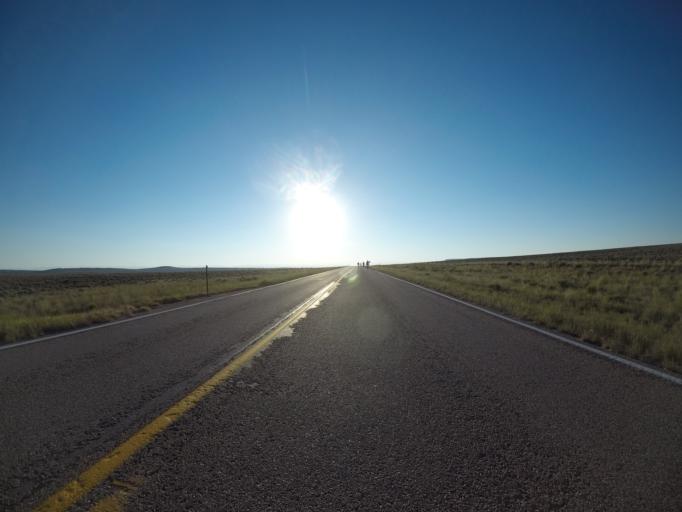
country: US
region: Wyoming
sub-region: Sublette County
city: Marbleton
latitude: 42.5790
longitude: -110.0051
